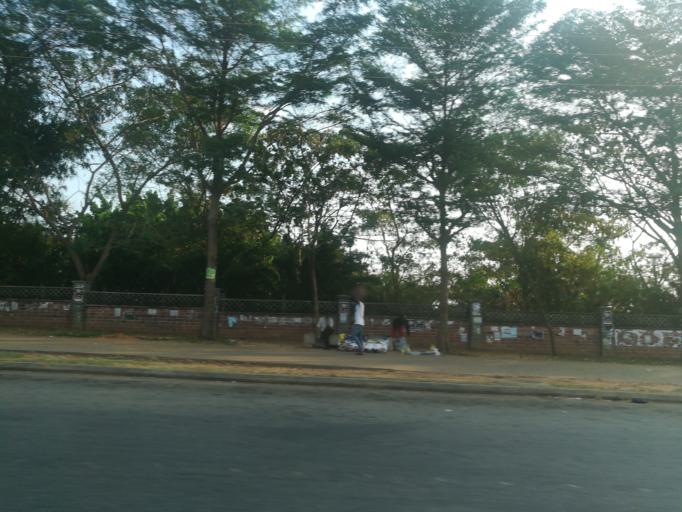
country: NG
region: Abuja Federal Capital Territory
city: Abuja
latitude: 9.0675
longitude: 7.4497
